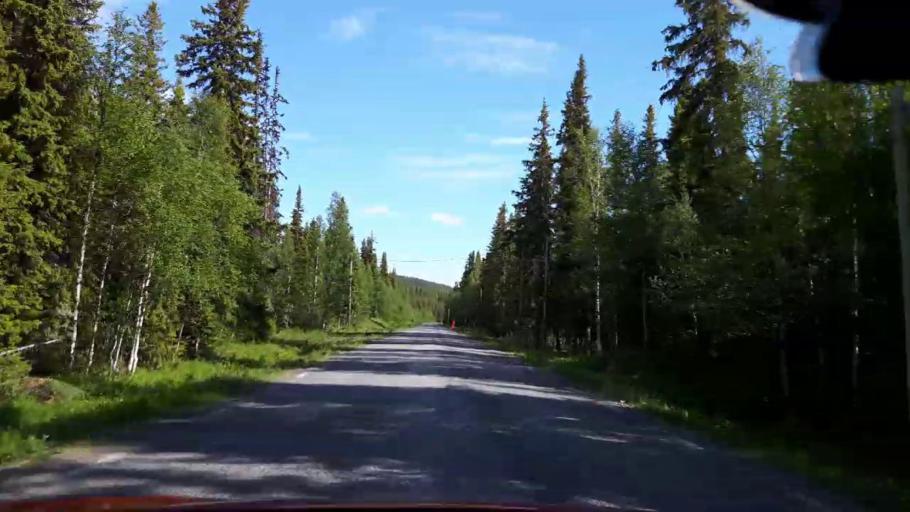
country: SE
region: Jaemtland
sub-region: Krokoms Kommun
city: Valla
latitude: 63.7552
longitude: 14.1099
